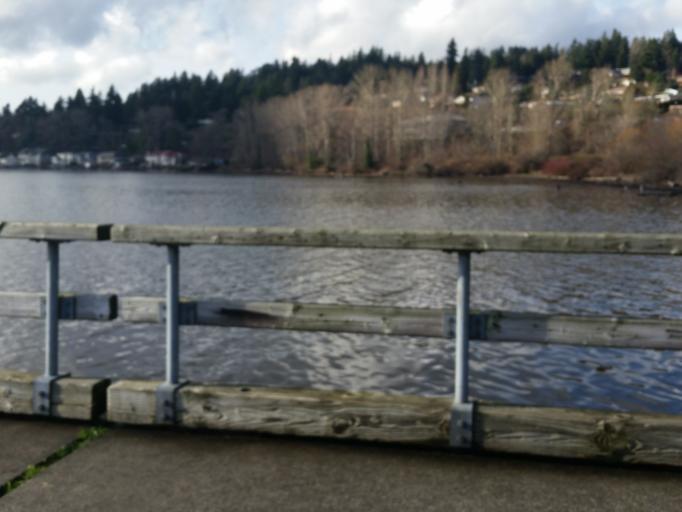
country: US
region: Washington
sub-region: King County
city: Lake Forest Park
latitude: 47.7568
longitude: -122.2634
